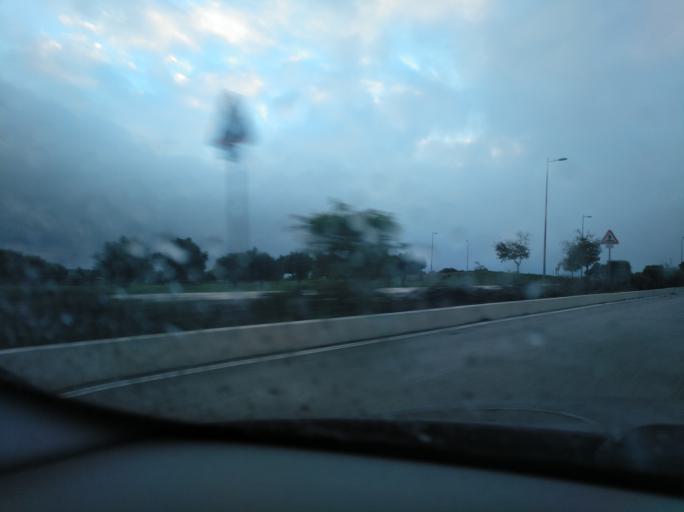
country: PT
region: Faro
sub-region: Castro Marim
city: Castro Marim
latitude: 37.2196
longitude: -7.4534
